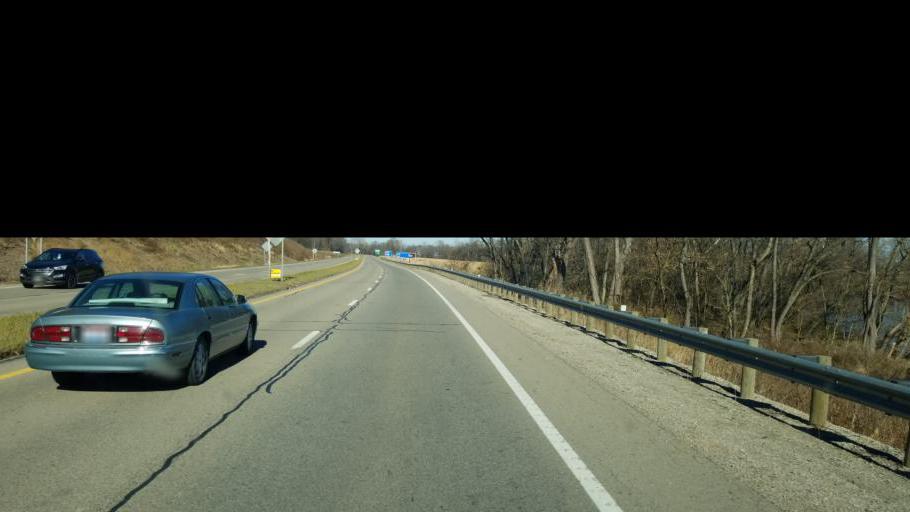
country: US
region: Ohio
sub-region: Coshocton County
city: Coshocton
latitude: 40.2509
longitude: -81.8728
